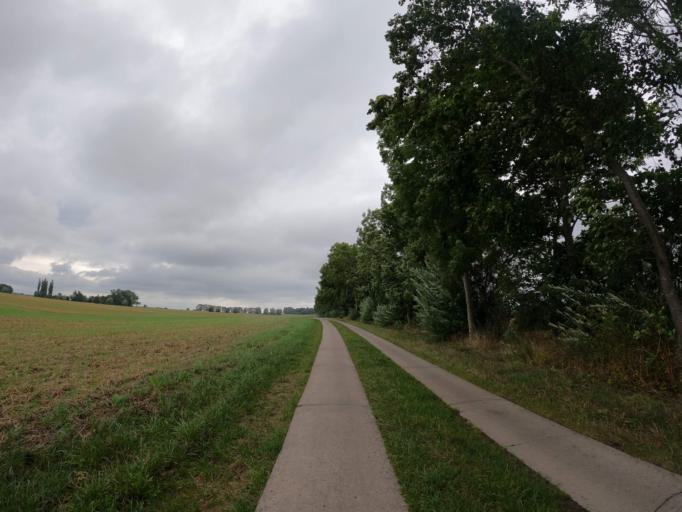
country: DE
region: Mecklenburg-Vorpommern
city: Garz
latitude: 54.2977
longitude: 13.3309
